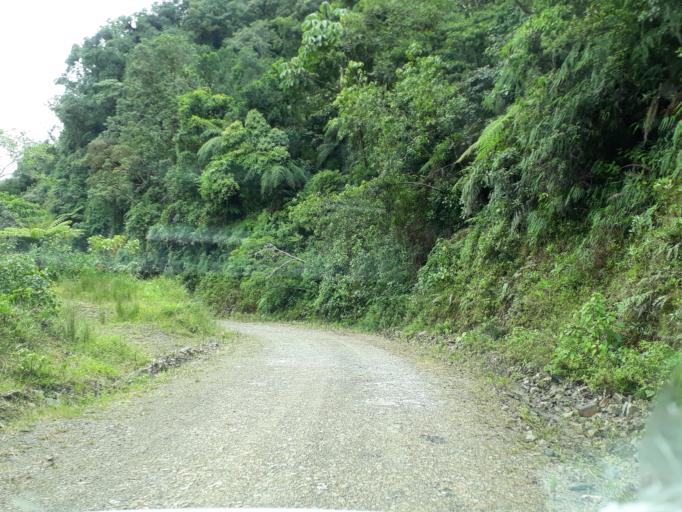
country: CO
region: Cundinamarca
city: Gachala
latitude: 4.7089
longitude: -73.3999
